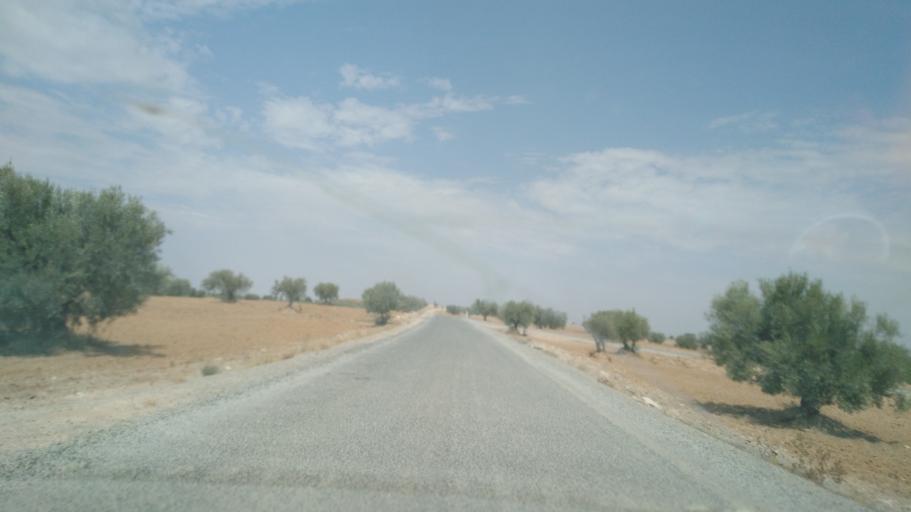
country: TN
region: Safaqis
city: Sfax
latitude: 34.7474
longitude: 10.5611
